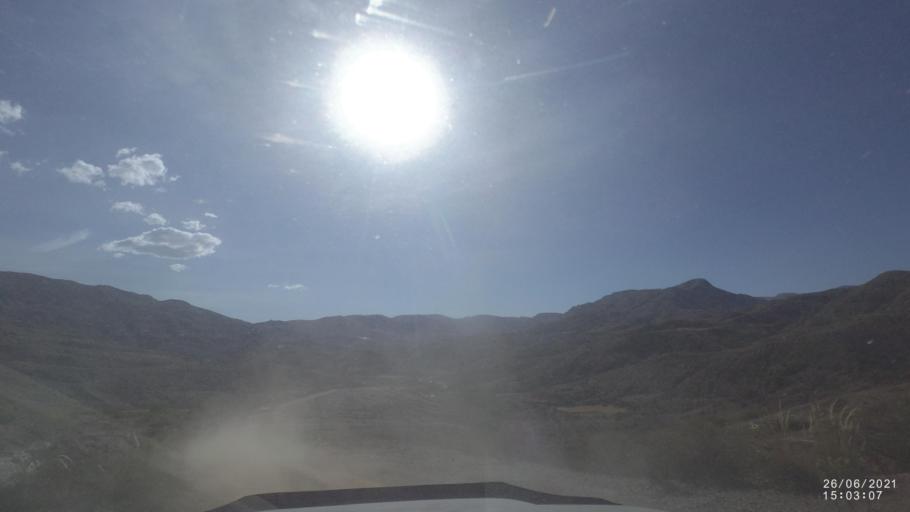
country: BO
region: Cochabamba
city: Mizque
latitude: -17.9494
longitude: -65.6279
